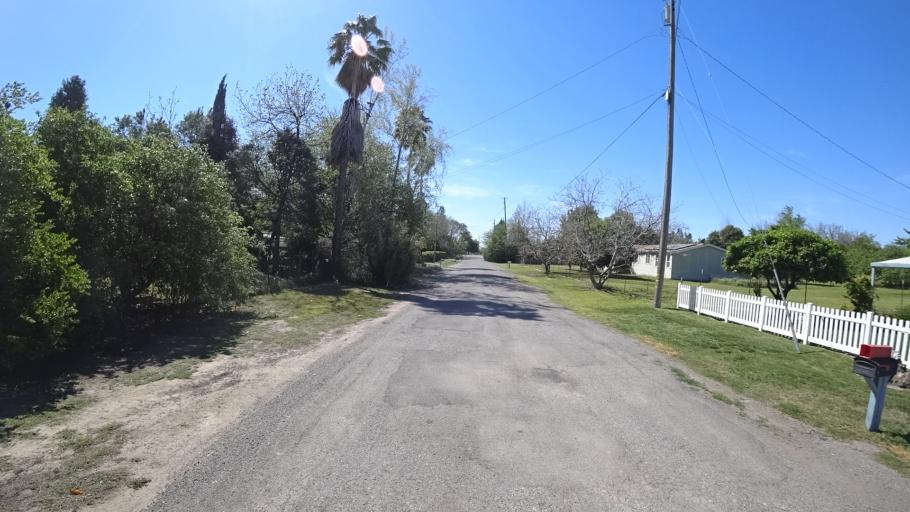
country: US
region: California
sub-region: Glenn County
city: Orland
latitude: 39.7484
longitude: -122.1382
